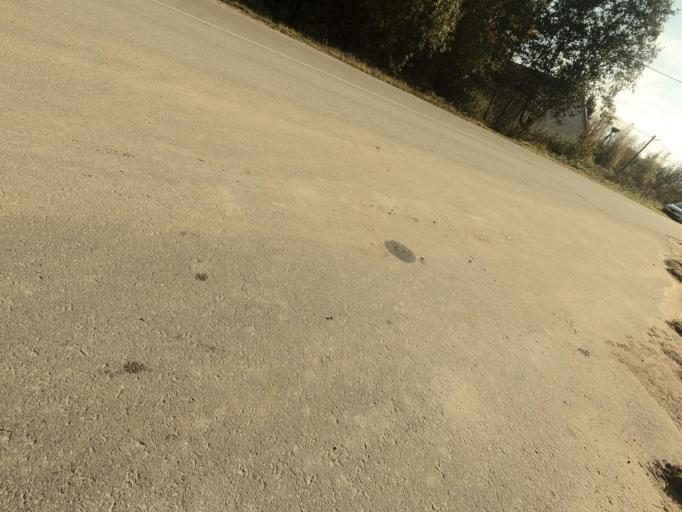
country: RU
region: Novgorod
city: Batetskiy
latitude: 58.7998
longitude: 30.6544
